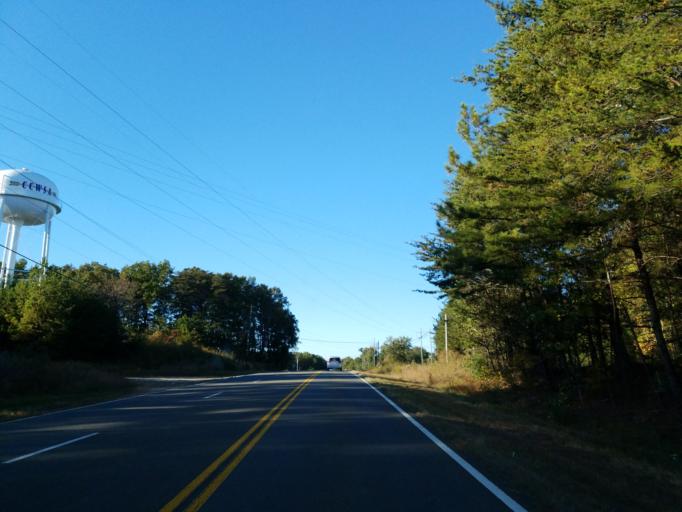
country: US
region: Georgia
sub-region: Pickens County
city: Nelson
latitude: 34.3982
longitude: -84.3827
